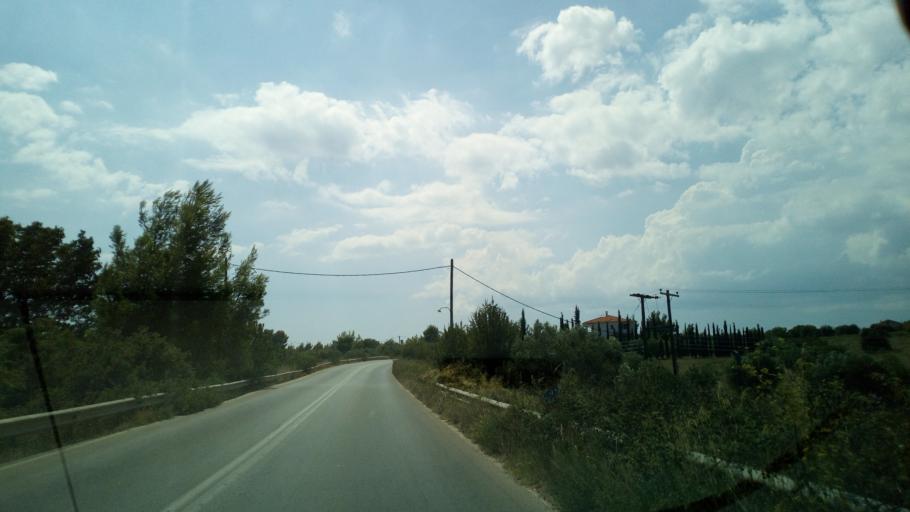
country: GR
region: Central Macedonia
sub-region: Nomos Chalkidikis
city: Nikiti
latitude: 40.2278
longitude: 23.6450
